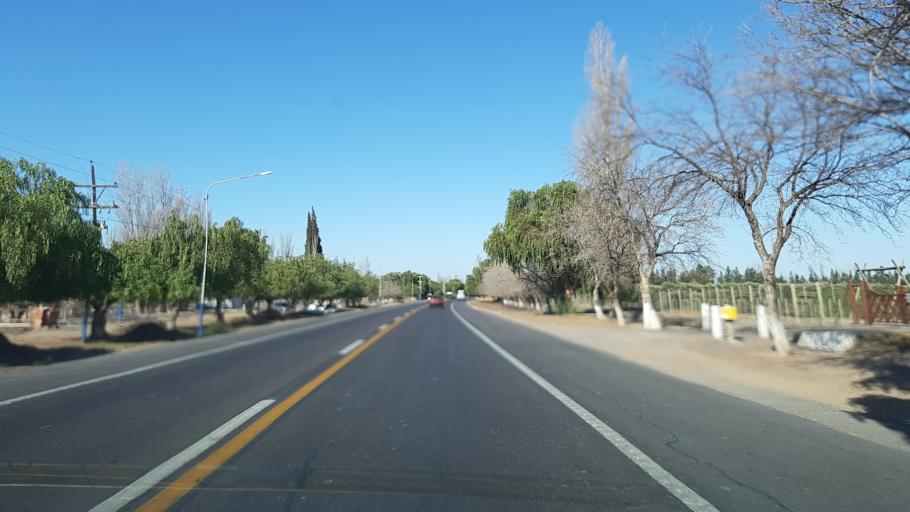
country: AR
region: San Juan
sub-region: Departamento de Santa Lucia
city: Santa Lucia
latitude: -31.5719
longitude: -68.4384
